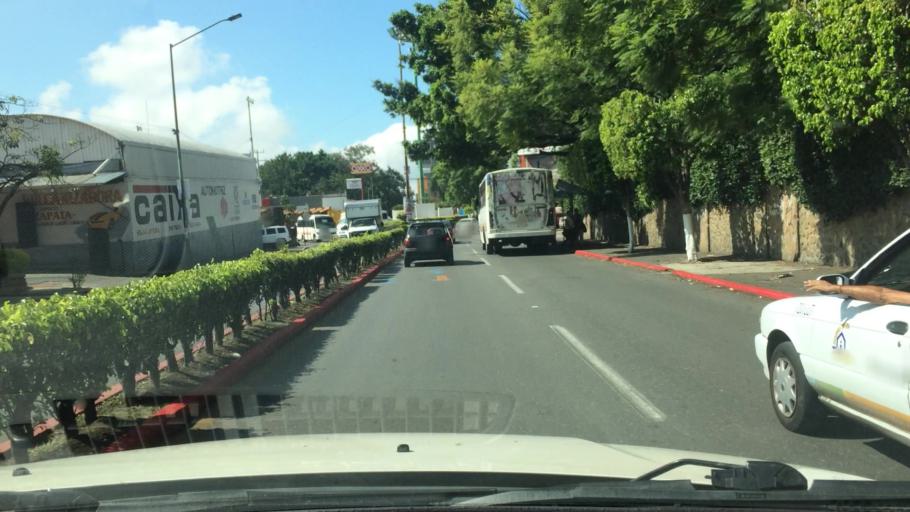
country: MX
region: Morelos
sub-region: Cuernavaca
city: Fraccionamiento Lomas de Ahuatlan
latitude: 18.9510
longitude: -99.2449
